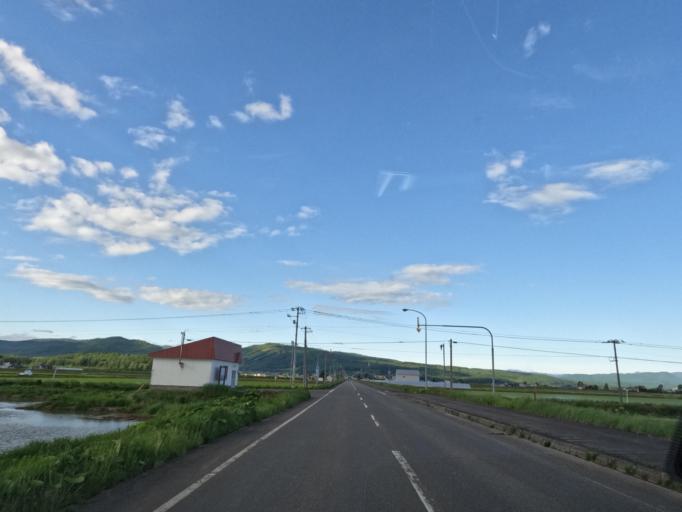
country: JP
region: Hokkaido
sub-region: Asahikawa-shi
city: Asahikawa
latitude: 43.8893
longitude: 142.4646
